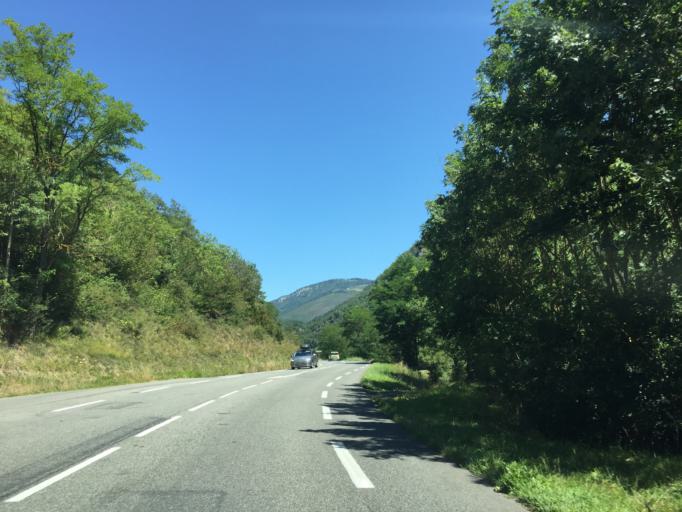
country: FR
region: Midi-Pyrenees
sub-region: Departement des Hautes-Pyrenees
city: Saint-Lary-Soulan
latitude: 42.8767
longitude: 0.3446
